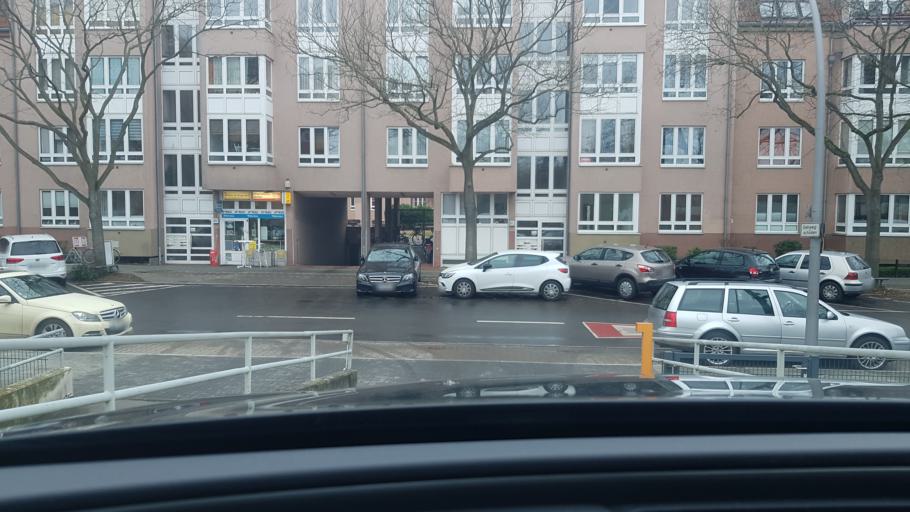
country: DE
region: Berlin
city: Mariendorf
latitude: 52.4324
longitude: 13.3832
